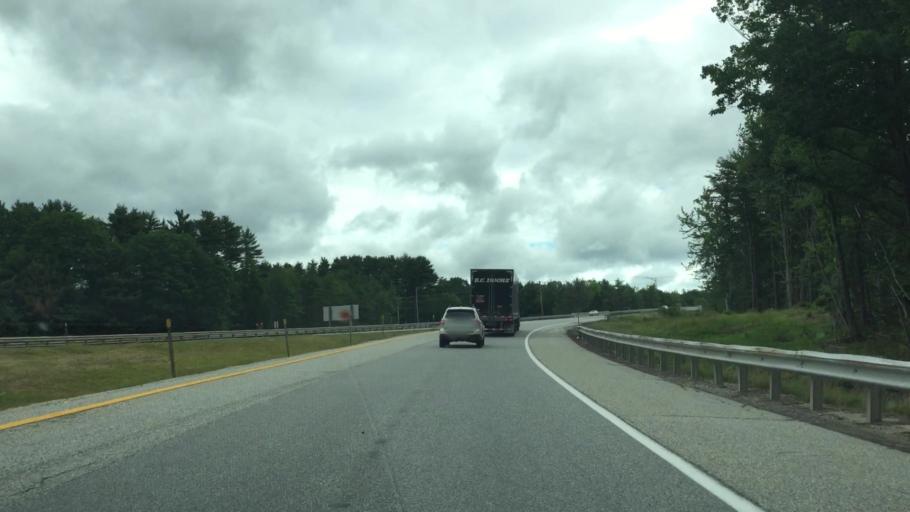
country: US
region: Maine
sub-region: Cumberland County
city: Falmouth
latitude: 43.7215
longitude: -70.3036
